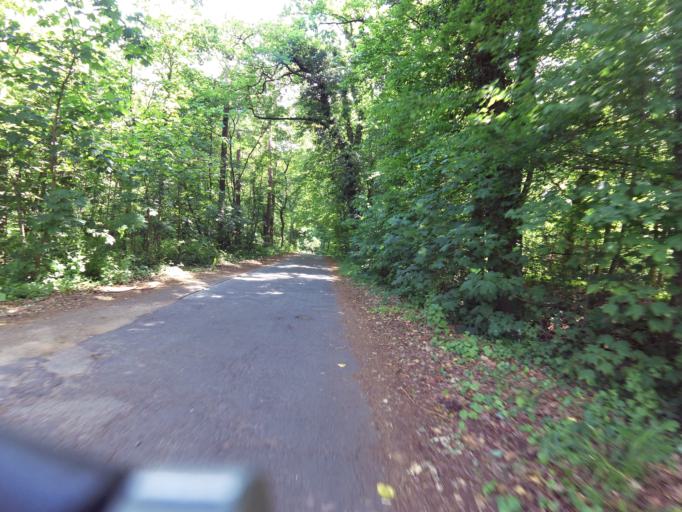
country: DE
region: Hesse
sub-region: Regierungsbezirk Darmstadt
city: Nauheim
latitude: 49.9536
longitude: 8.4695
